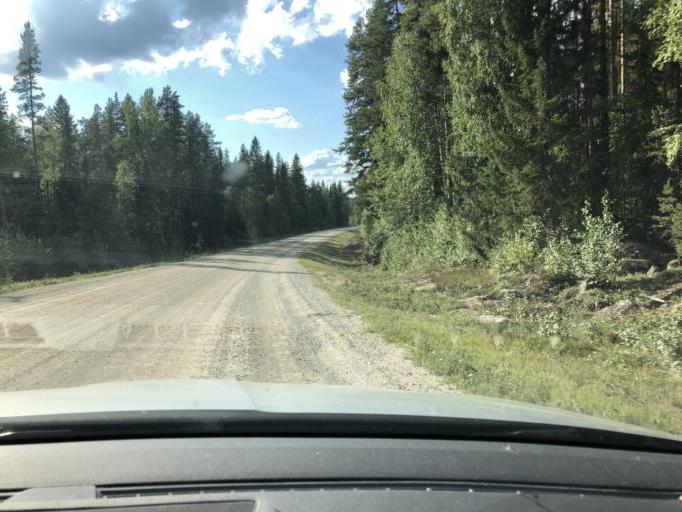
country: SE
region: Vaesternorrland
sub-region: Solleftea Kommun
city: Solleftea
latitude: 63.3119
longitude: 17.2693
